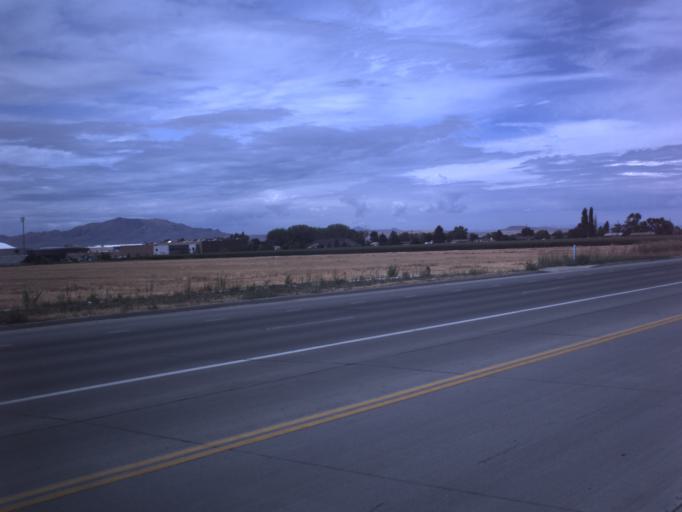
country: US
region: Utah
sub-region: Davis County
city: Syracuse
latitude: 41.1106
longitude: -112.0569
